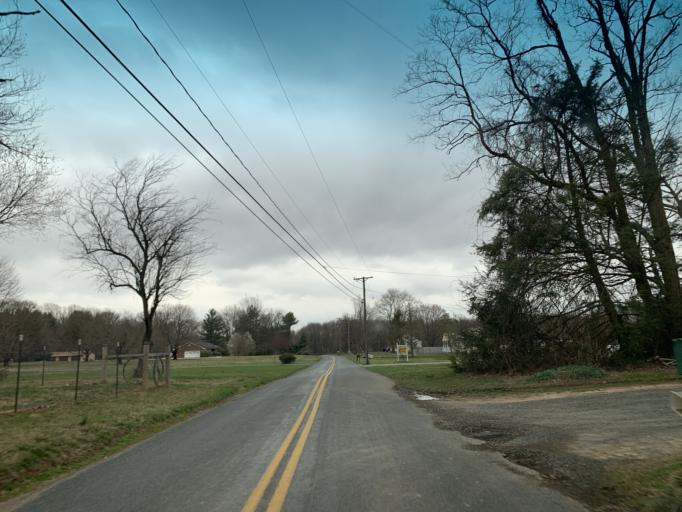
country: US
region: Maryland
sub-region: Harford County
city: Aberdeen
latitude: 39.5717
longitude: -76.1975
